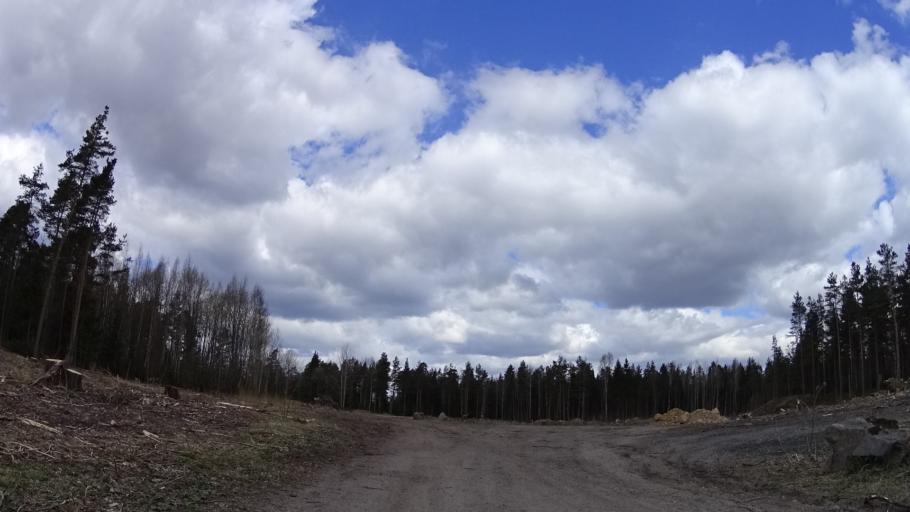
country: FI
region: Uusimaa
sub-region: Helsinki
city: Kilo
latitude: 60.2308
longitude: 24.8004
